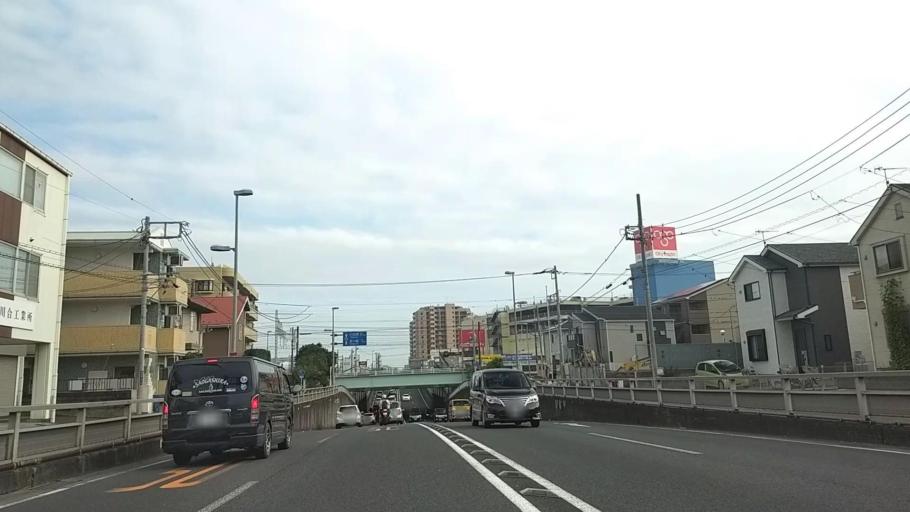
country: JP
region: Kanagawa
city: Hiratsuka
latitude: 35.3307
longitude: 139.3594
